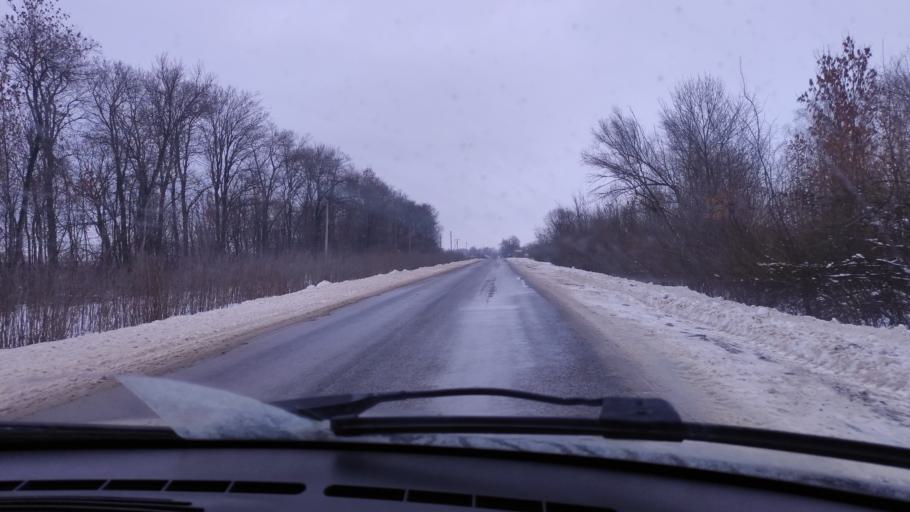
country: RU
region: Tambov
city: Pervomayskiy
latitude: 53.3014
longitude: 40.3638
